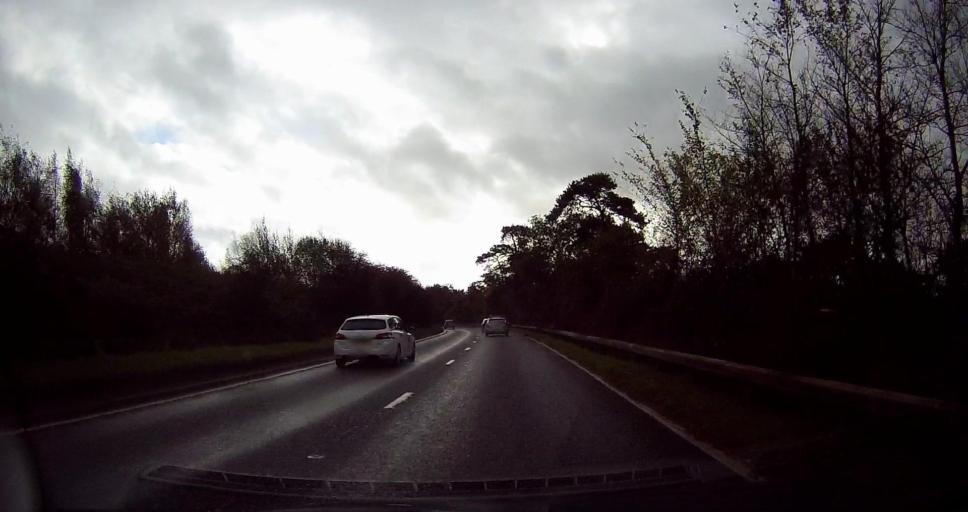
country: GB
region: England
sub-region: Staffordshire
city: Shenstone
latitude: 52.6141
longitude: -1.7978
